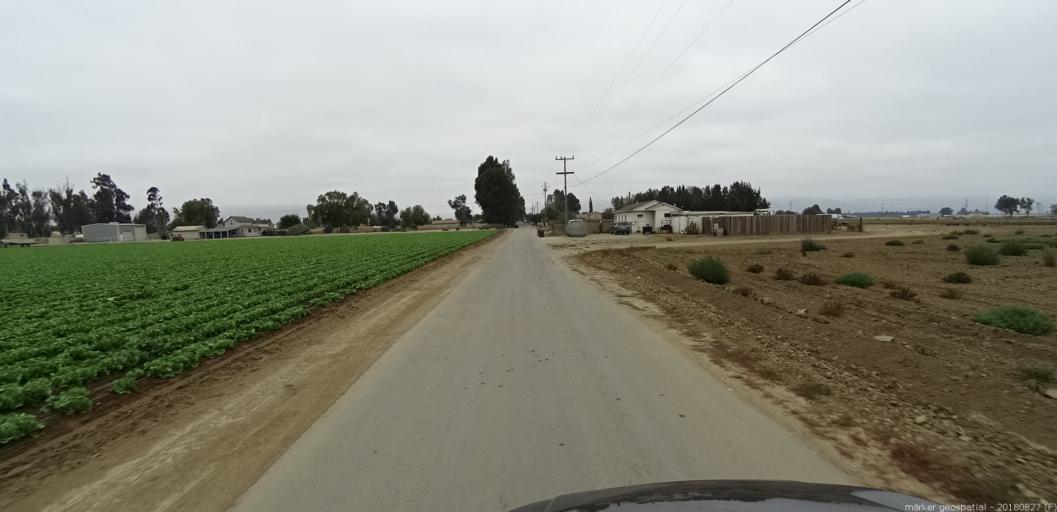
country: US
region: California
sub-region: Monterey County
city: Greenfield
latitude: 36.3339
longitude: -121.2443
